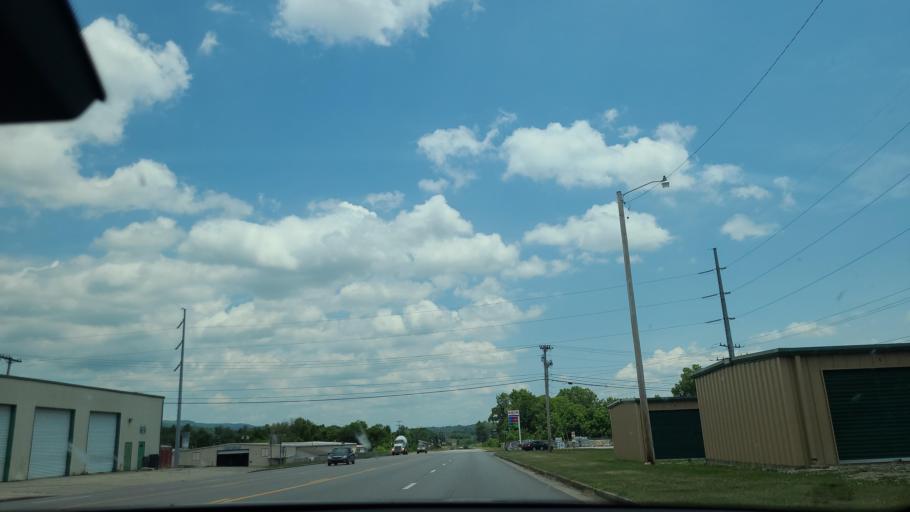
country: US
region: Tennessee
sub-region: Bledsoe County
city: Pikeville
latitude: 35.6093
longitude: -85.1947
